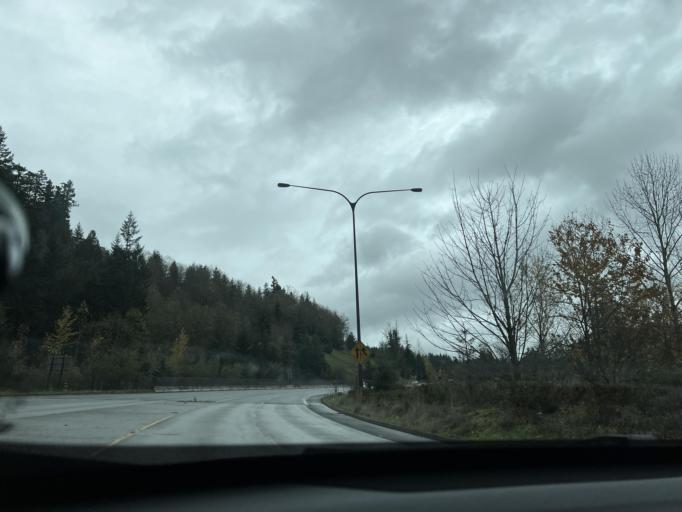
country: US
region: Washington
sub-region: King County
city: Issaquah
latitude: 47.5327
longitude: -122.0224
